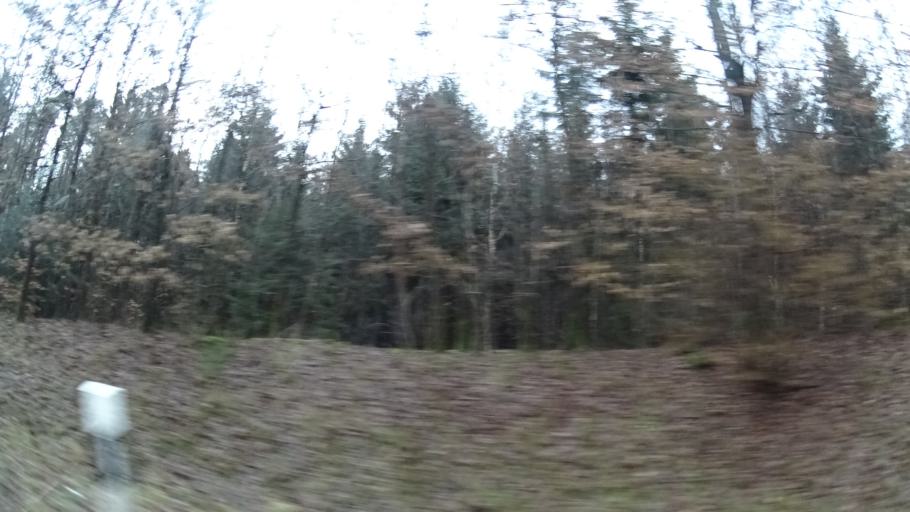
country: DE
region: Hesse
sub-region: Regierungsbezirk Kassel
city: Neuhof
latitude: 50.4617
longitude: 9.6537
